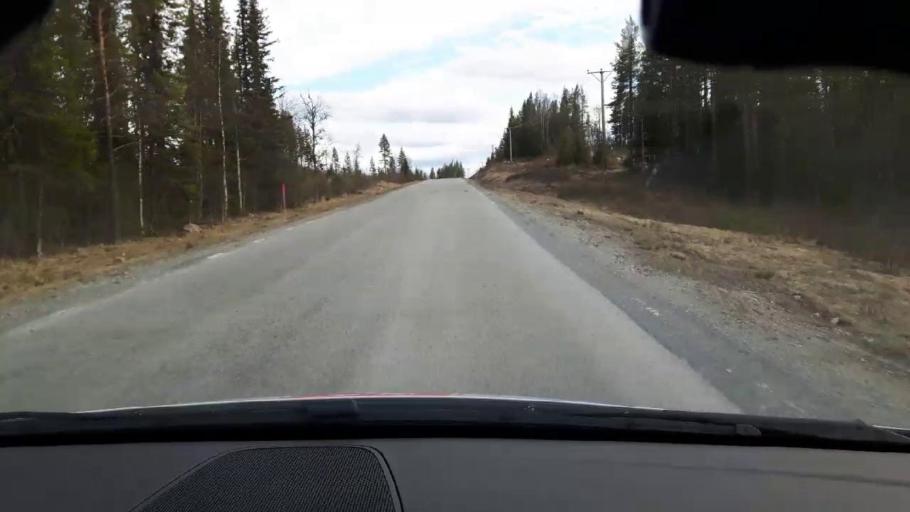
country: SE
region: Jaemtland
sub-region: Bergs Kommun
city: Hoverberg
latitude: 62.6992
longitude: 14.6232
